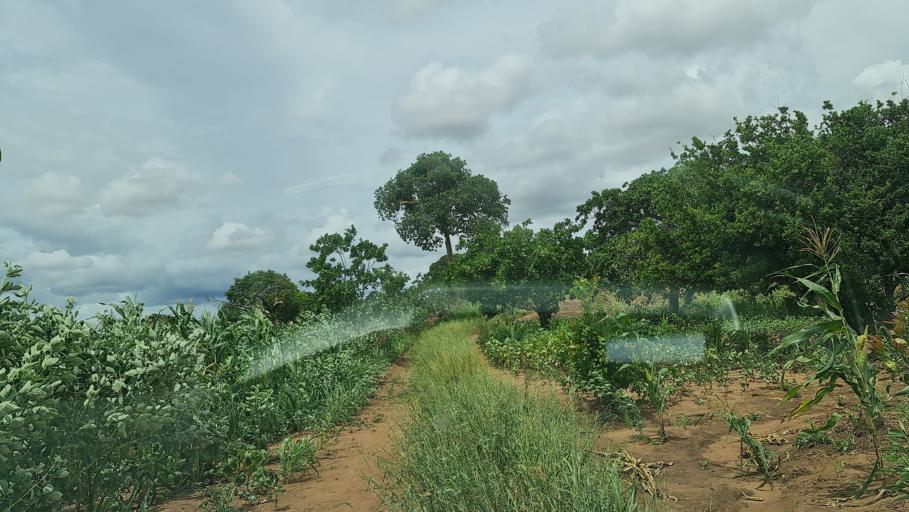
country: MZ
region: Nampula
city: Nacala
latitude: -14.7814
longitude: 39.9842
